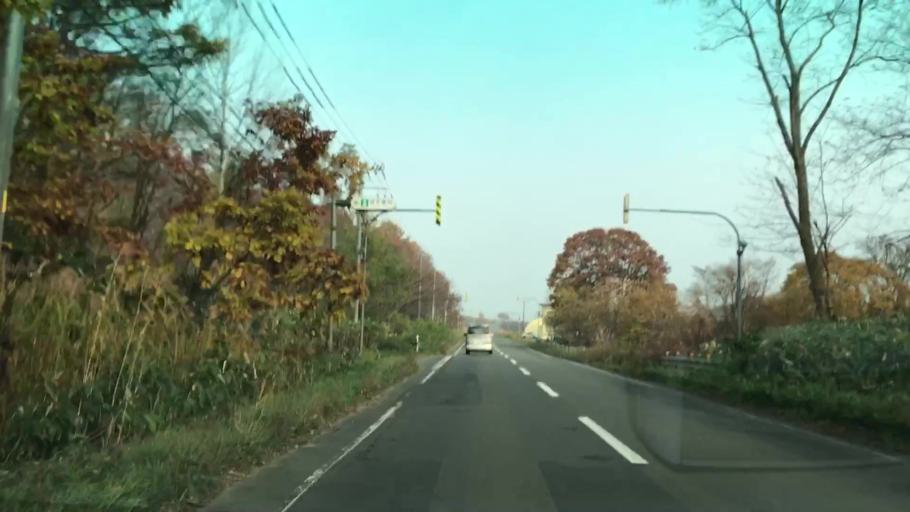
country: JP
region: Hokkaido
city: Ishikari
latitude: 43.3271
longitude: 141.4424
